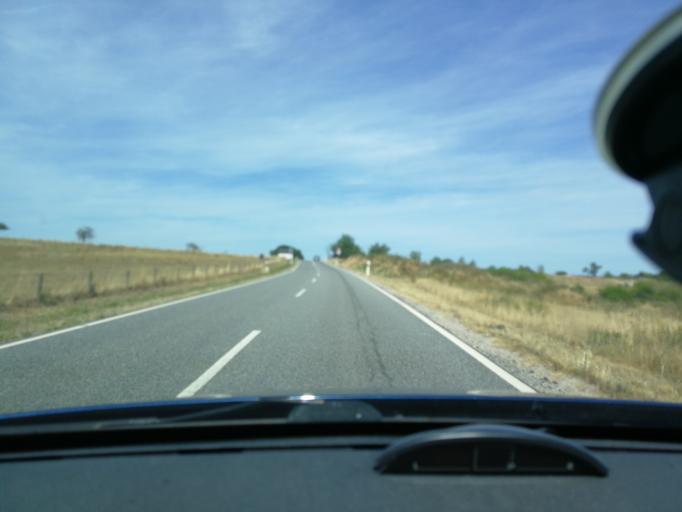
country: DE
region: Rheinland-Pfalz
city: Arenrath
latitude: 49.9472
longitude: 6.7415
